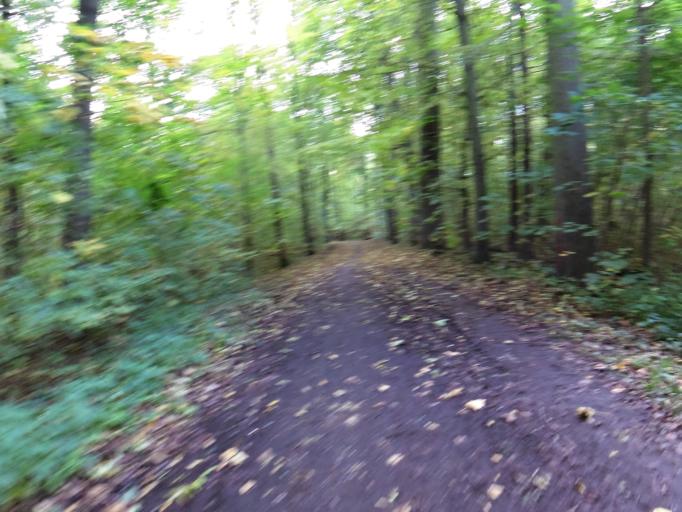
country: DE
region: Saxony
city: Markkleeberg
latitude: 51.3052
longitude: 12.3566
